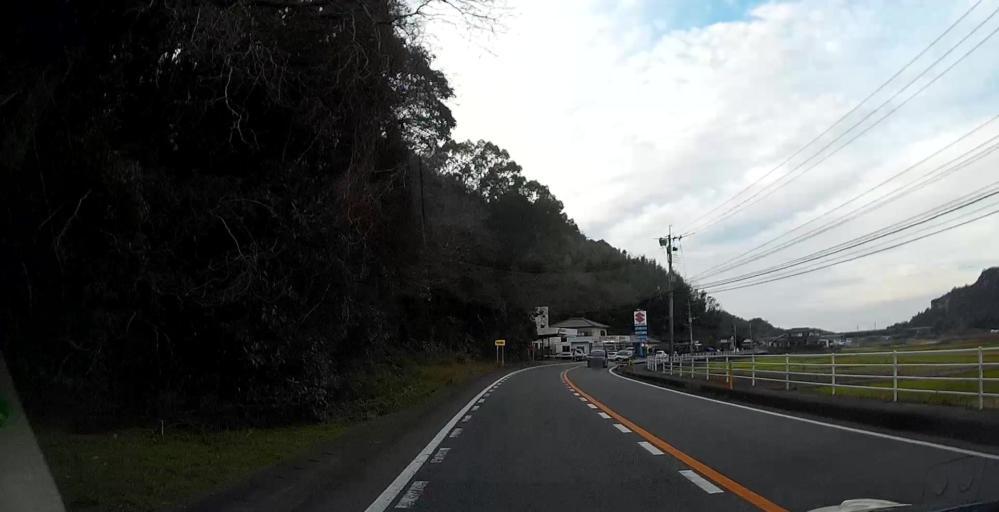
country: JP
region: Kumamoto
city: Yatsushiro
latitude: 32.4979
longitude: 130.4057
